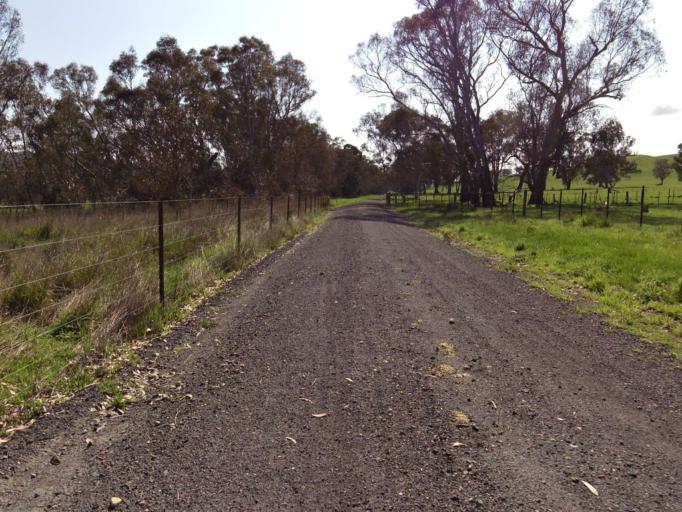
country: AU
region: Victoria
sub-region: Murrindindi
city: Alexandra
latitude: -37.1430
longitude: 145.5889
